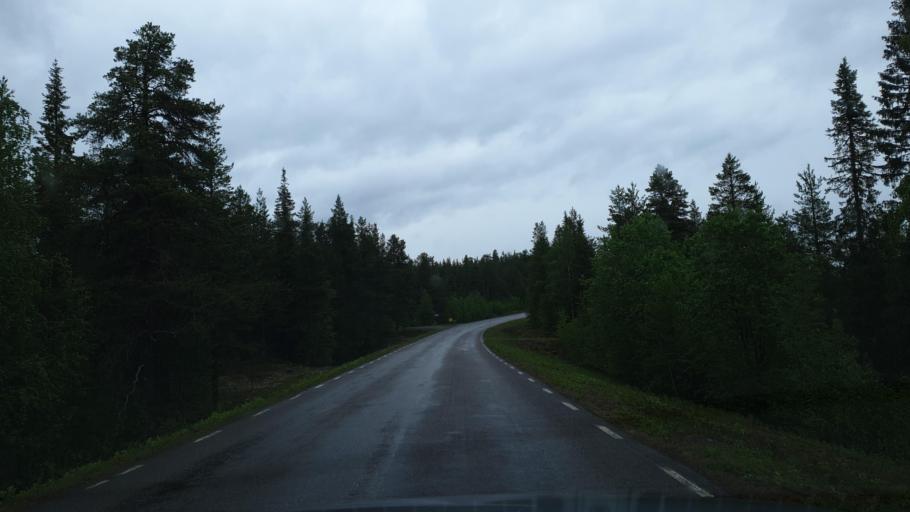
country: SE
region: Norrbotten
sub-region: Kiruna Kommun
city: Kiruna
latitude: 67.8875
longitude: 21.0158
